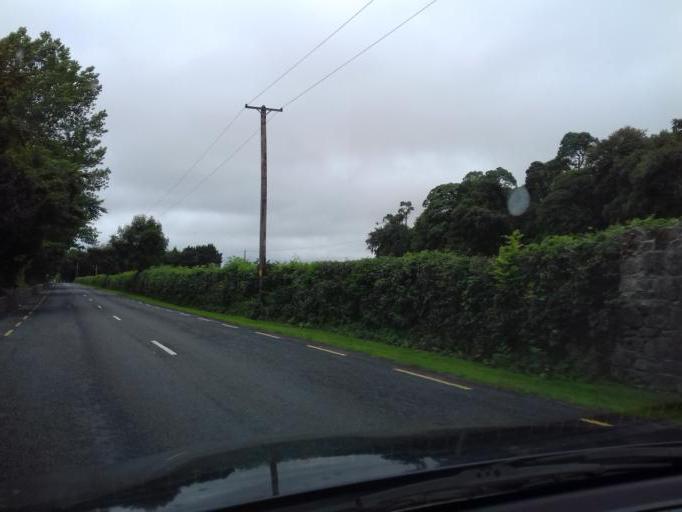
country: IE
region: Leinster
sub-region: County Carlow
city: Bagenalstown
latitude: 52.7127
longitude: -6.9565
